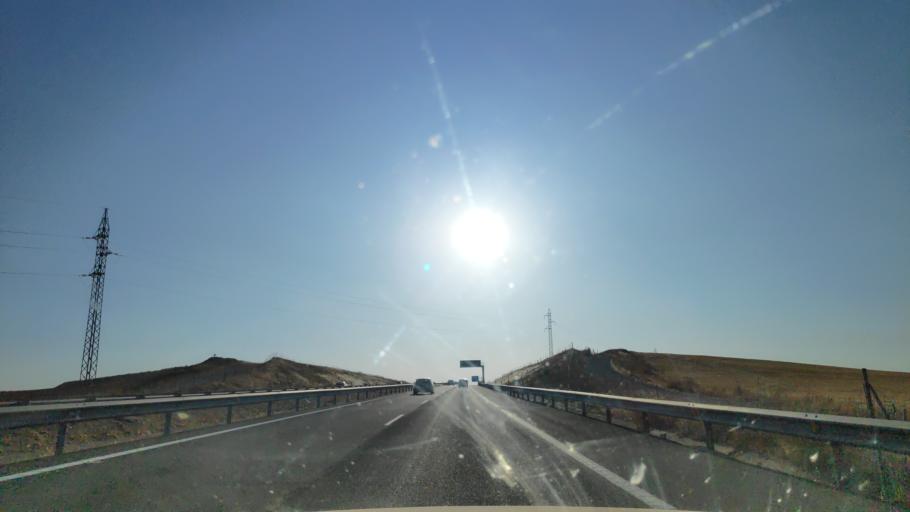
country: ES
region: Castille-La Mancha
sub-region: Provincia de Cuenca
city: Tarancon
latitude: 39.9924
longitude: -2.9938
